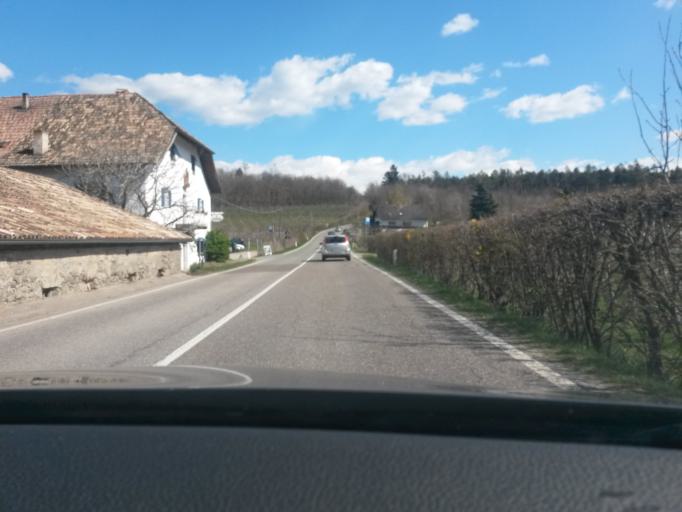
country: IT
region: Trentino-Alto Adige
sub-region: Bolzano
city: San Michele
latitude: 46.4427
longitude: 11.2759
